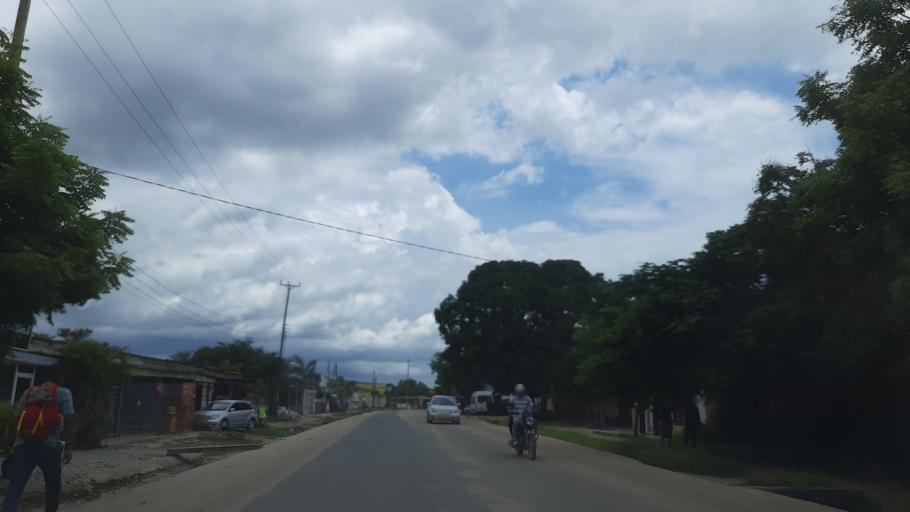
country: TZ
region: Dar es Salaam
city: Magomeni
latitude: -6.7765
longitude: 39.2345
